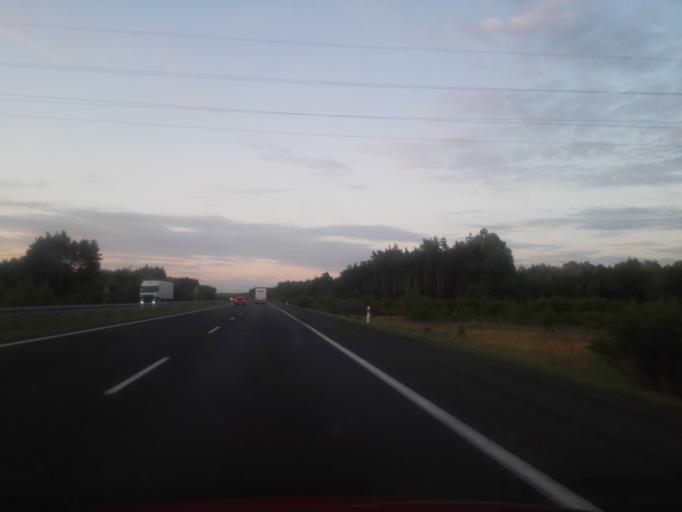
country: PL
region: Silesian Voivodeship
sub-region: Powiat czestochowski
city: Klomnice
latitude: 51.0326
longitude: 19.3341
